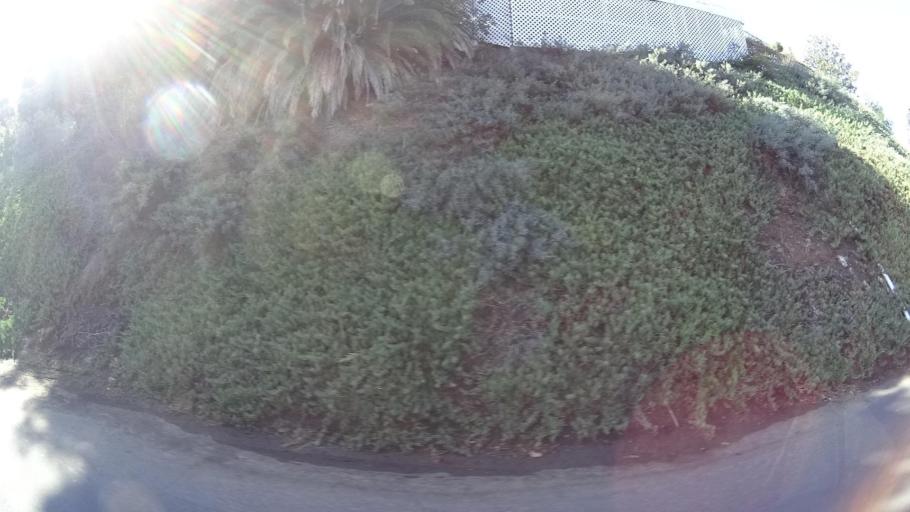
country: US
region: California
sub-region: San Diego County
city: Casa de Oro-Mount Helix
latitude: 32.7690
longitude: -116.9839
